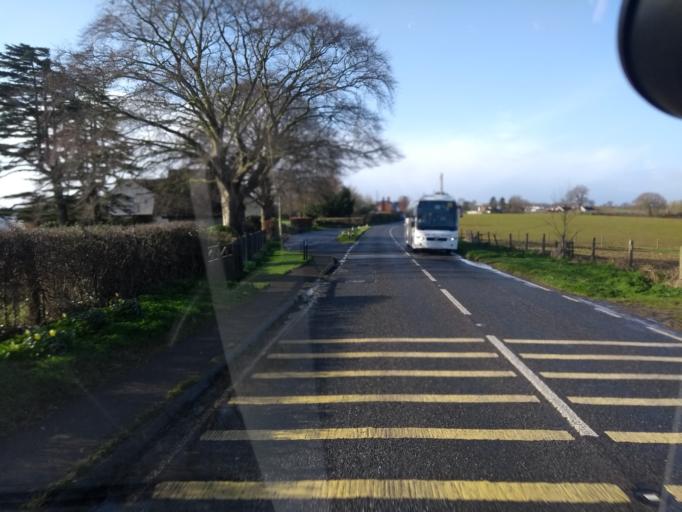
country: GB
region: England
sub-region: Somerset
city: Yeovil
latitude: 50.9713
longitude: -2.6113
